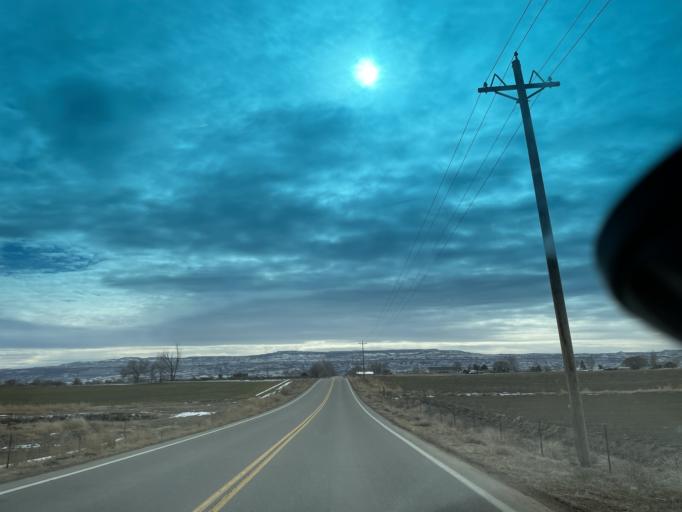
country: US
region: Colorado
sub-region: Mesa County
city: Loma
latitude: 39.2159
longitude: -108.8129
